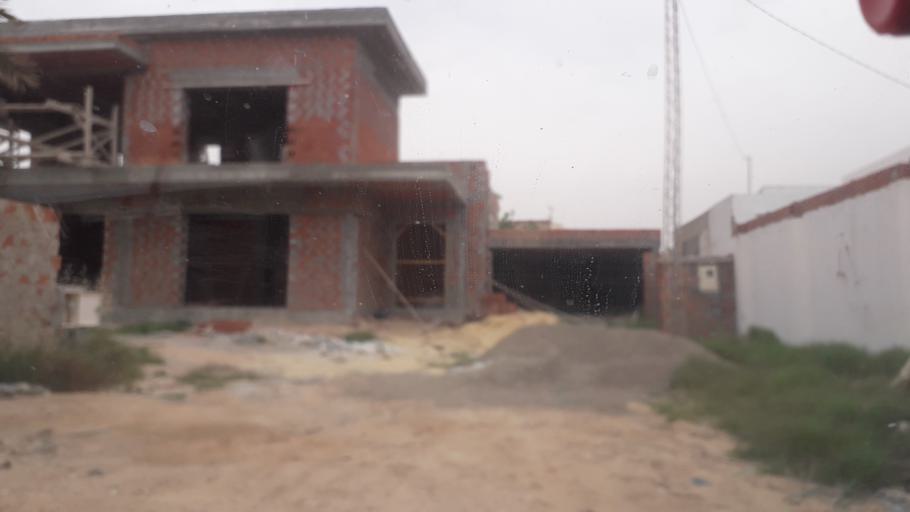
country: TN
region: Safaqis
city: Al Qarmadah
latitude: 34.7951
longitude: 10.7649
